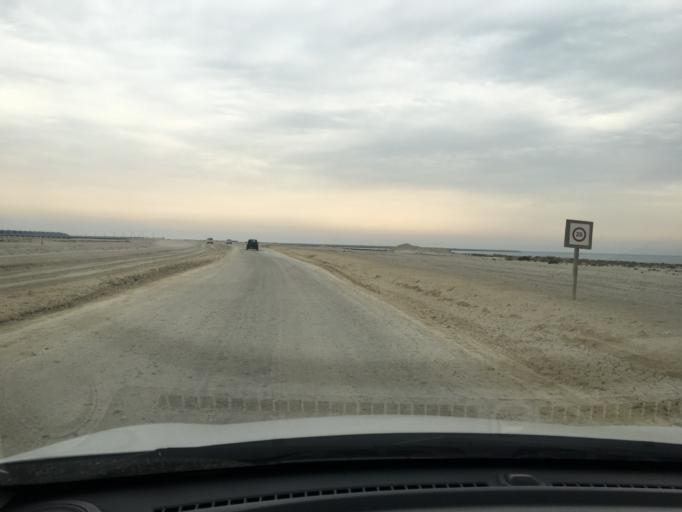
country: BH
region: Central Governorate
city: Dar Kulayb
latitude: 25.8323
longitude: 50.5939
